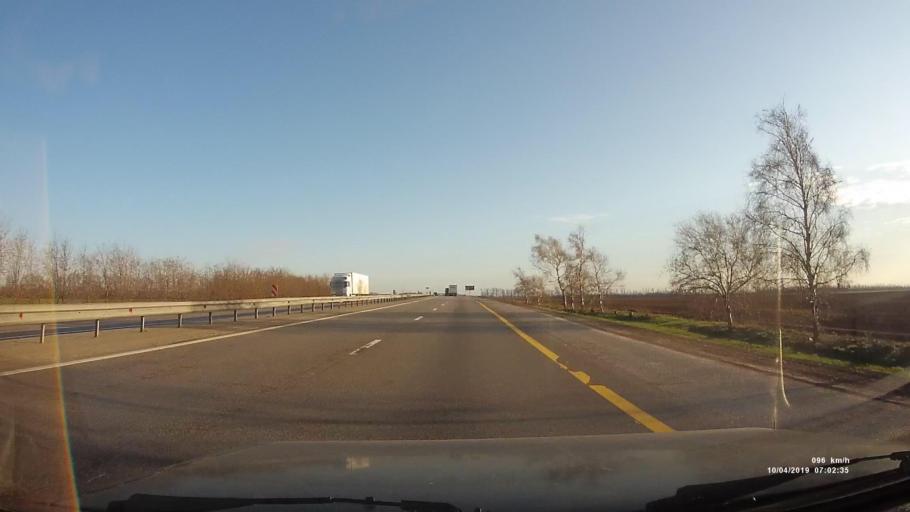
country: RU
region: Rostov
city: Krasyukovskaya
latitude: 47.6100
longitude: 39.9937
